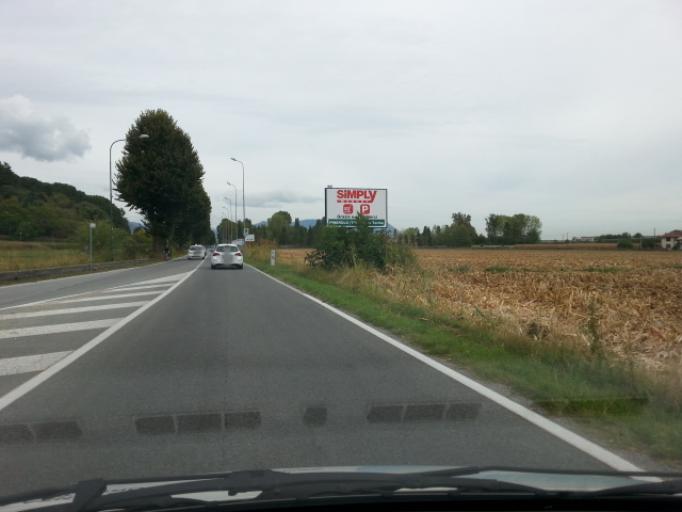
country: IT
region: Piedmont
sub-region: Provincia di Torino
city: Pinerolo
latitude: 44.8944
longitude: 7.3555
